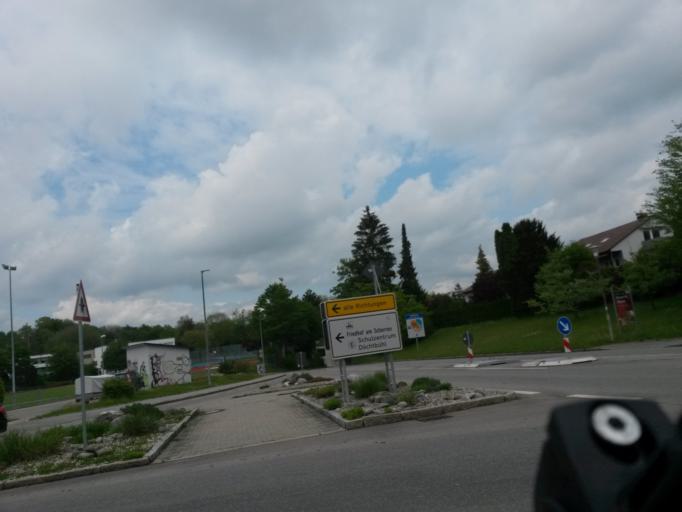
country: DE
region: Baden-Wuerttemberg
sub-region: Tuebingen Region
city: Bad Waldsee
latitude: 47.9140
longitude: 9.7566
